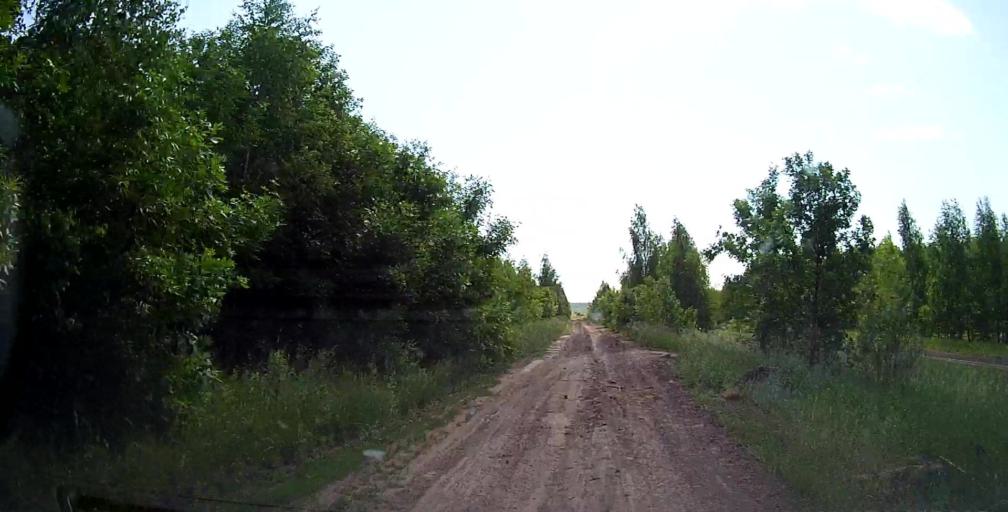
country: RU
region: Tula
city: Kurkino
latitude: 53.1684
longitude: 38.4878
